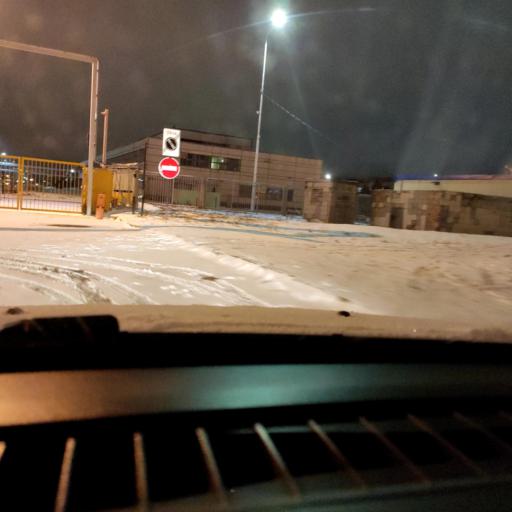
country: RU
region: Samara
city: Tol'yatti
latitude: 53.5616
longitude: 49.2864
